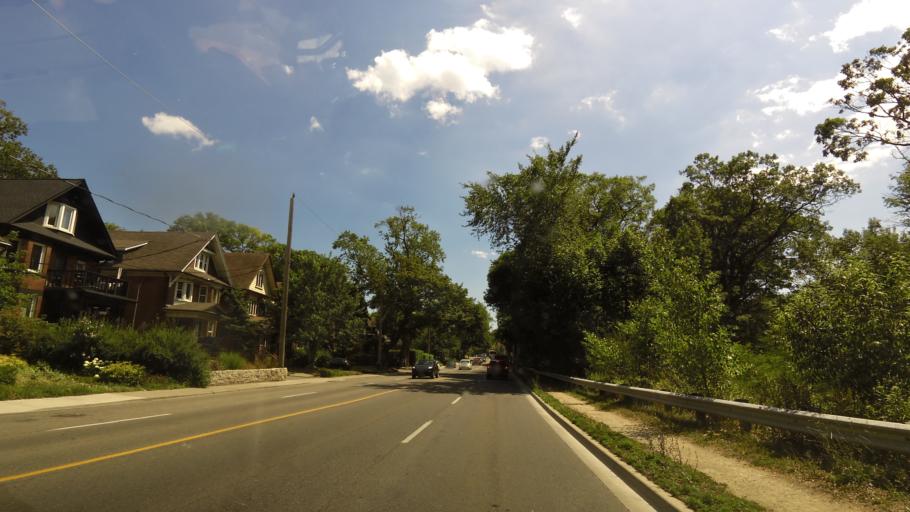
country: CA
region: Ontario
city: Toronto
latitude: 43.6507
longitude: -79.4584
